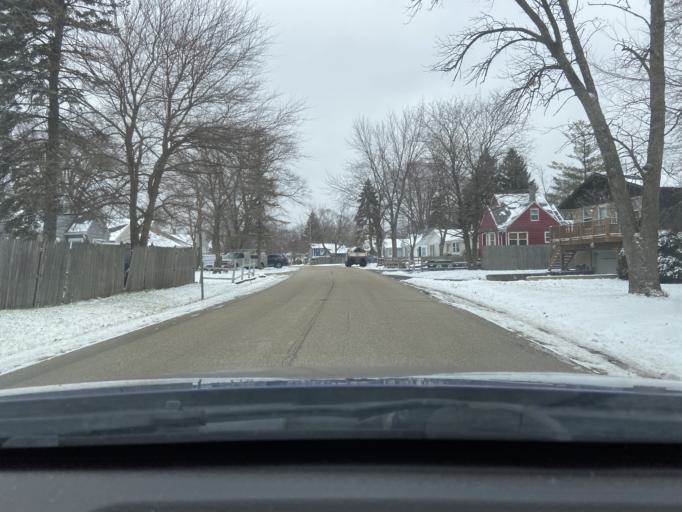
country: US
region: Illinois
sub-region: Lake County
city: Round Lake Park
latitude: 42.3501
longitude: -88.0800
